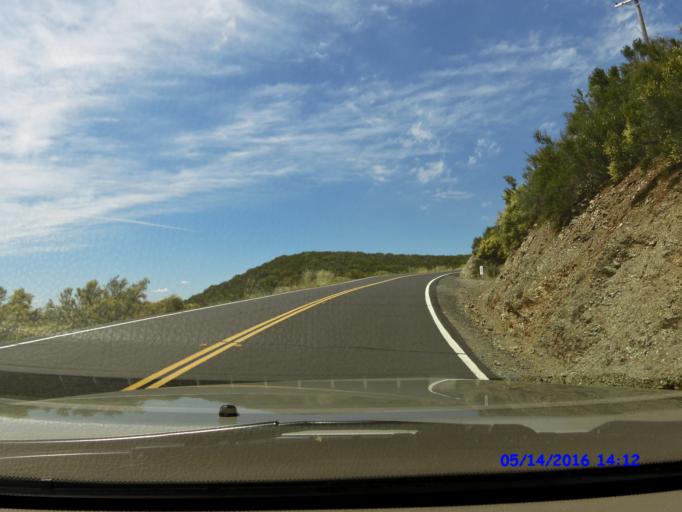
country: US
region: California
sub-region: Mariposa County
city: Mariposa
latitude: 37.6384
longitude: -120.1521
